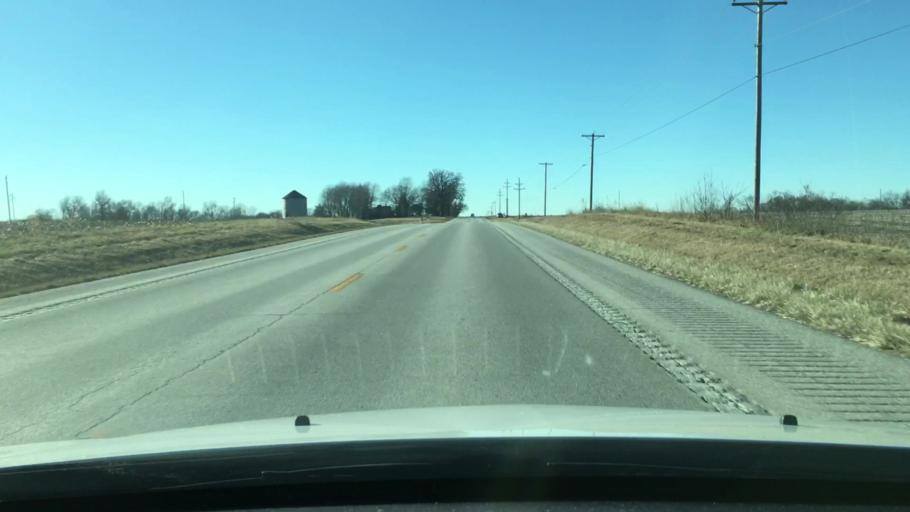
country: US
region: Missouri
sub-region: Pike County
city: Bowling Green
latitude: 39.3444
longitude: -91.2755
